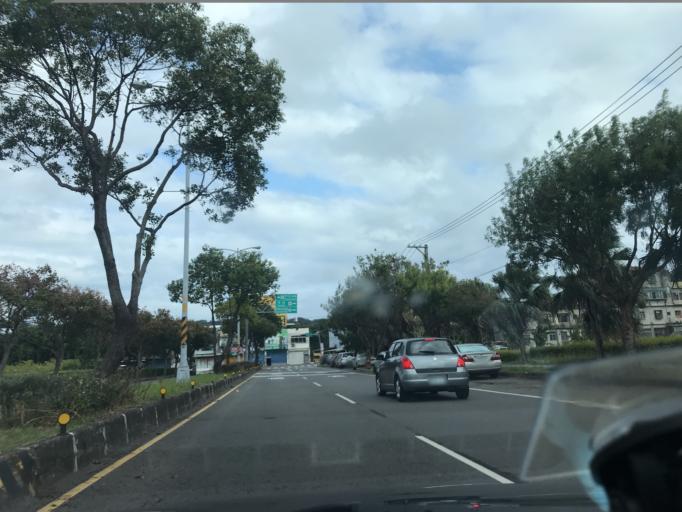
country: TW
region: Taiwan
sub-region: Hsinchu
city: Zhubei
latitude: 24.8037
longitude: 121.0488
